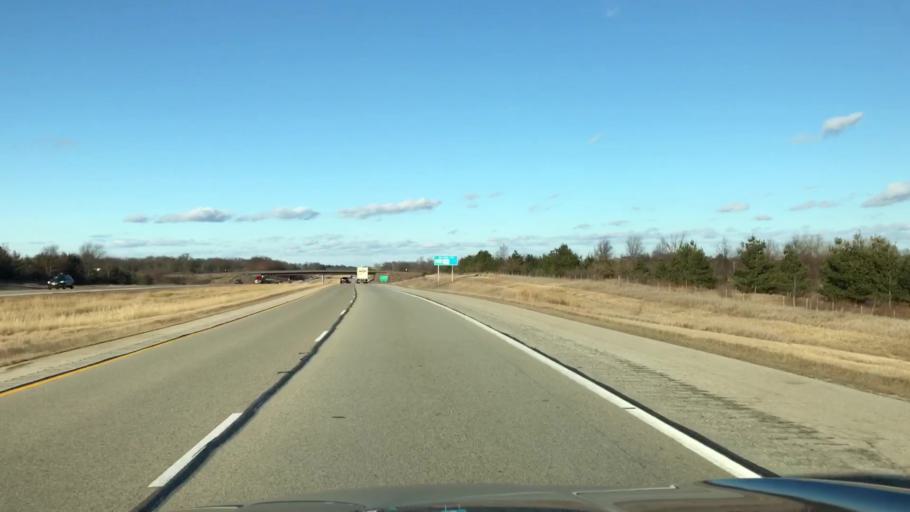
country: US
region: Illinois
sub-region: McLean County
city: Lexington
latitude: 40.6212
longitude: -88.8187
